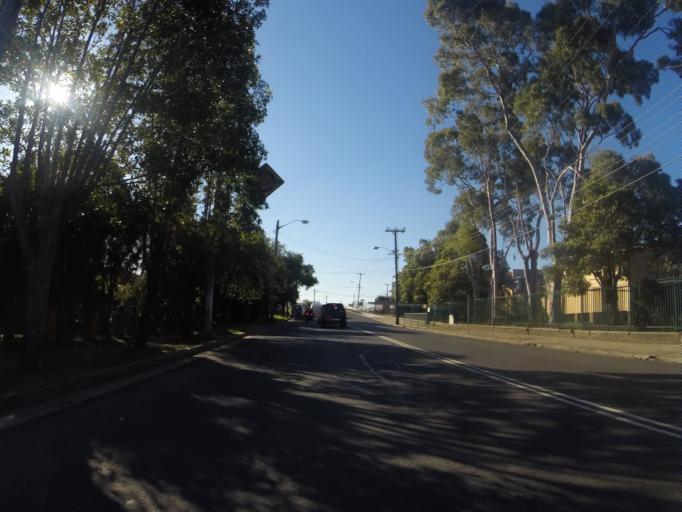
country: AU
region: New South Wales
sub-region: Bankstown
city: Regents Park
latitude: -33.8851
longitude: 151.0235
